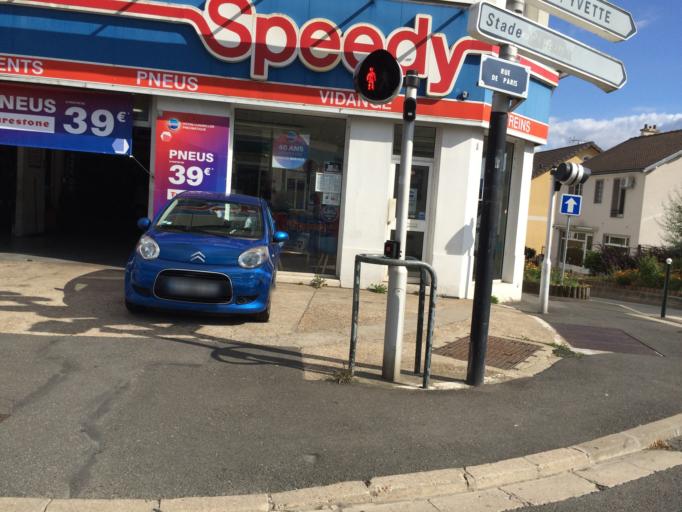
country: FR
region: Ile-de-France
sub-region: Departement de l'Essonne
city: Villebon-sur-Yvette
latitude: 48.7069
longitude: 2.2391
